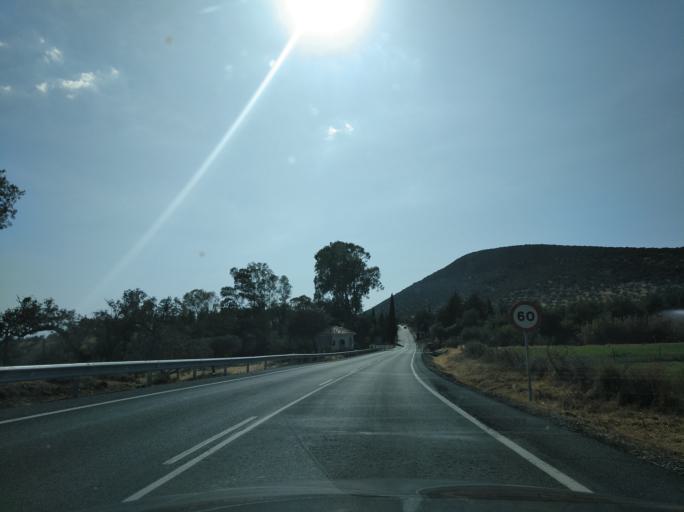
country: ES
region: Andalusia
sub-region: Provincia de Huelva
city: Rosal de la Frontera
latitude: 37.9602
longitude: -7.2501
